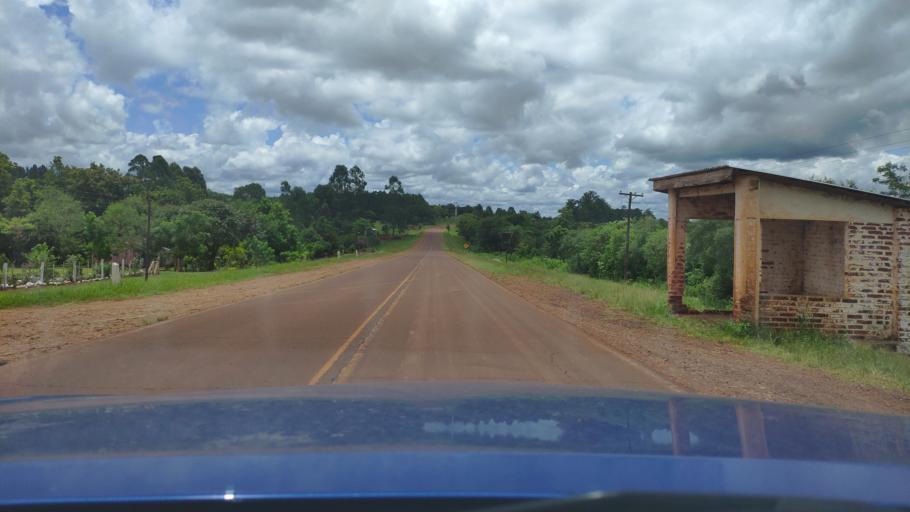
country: AR
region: Misiones
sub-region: Departamento de San Javier
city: San Javier
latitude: -27.8604
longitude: -55.2538
